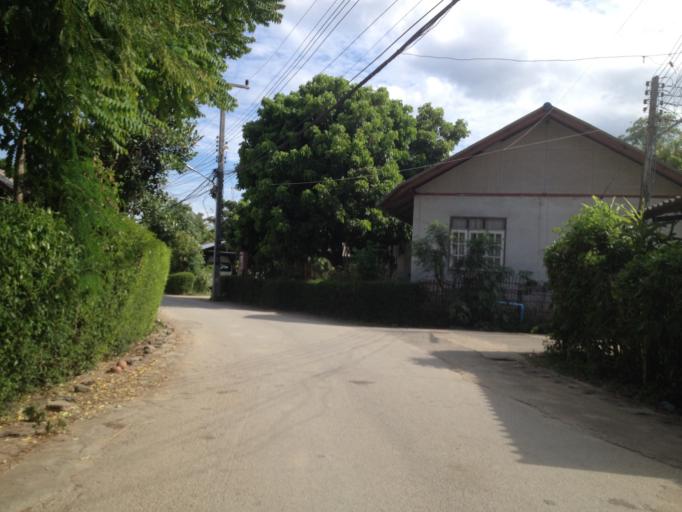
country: TH
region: Chiang Mai
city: Hang Dong
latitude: 18.7188
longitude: 98.9187
